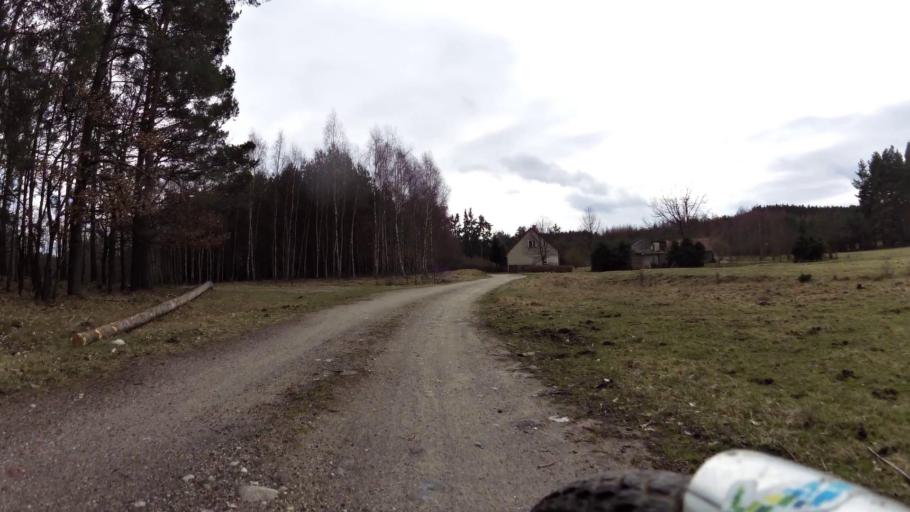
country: PL
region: Pomeranian Voivodeship
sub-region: Powiat bytowski
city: Kolczyglowy
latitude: 54.1556
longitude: 17.1870
